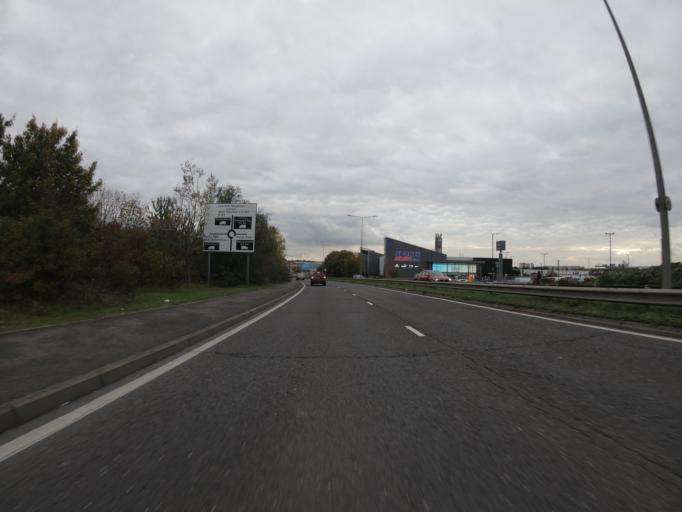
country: GB
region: England
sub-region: Kent
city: West Thurrock
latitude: 51.4872
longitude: 0.2729
